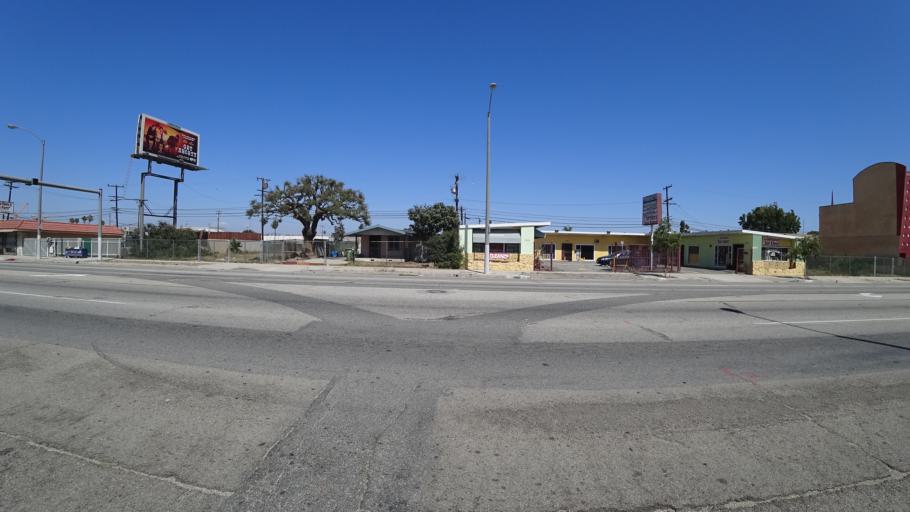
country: US
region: California
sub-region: Los Angeles County
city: Lennox
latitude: 33.9427
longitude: -118.3440
